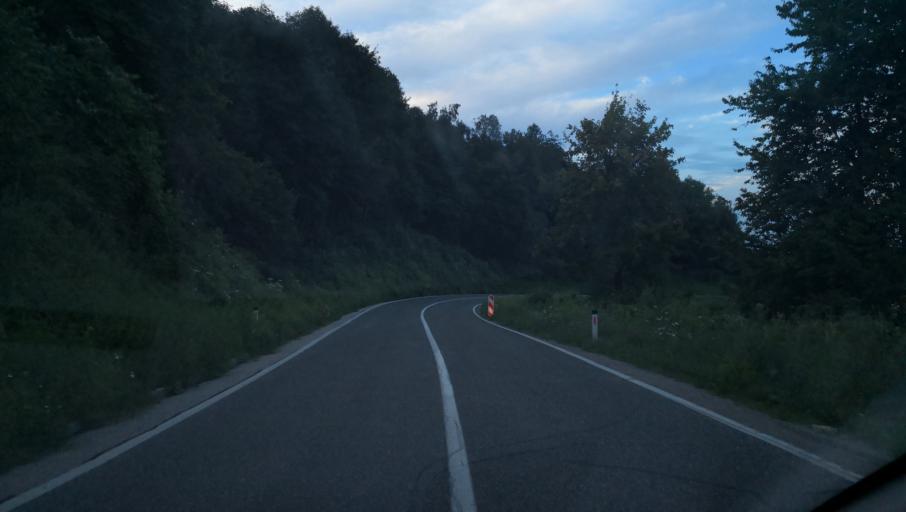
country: SI
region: Semic
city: Semic
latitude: 45.7153
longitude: 15.2317
